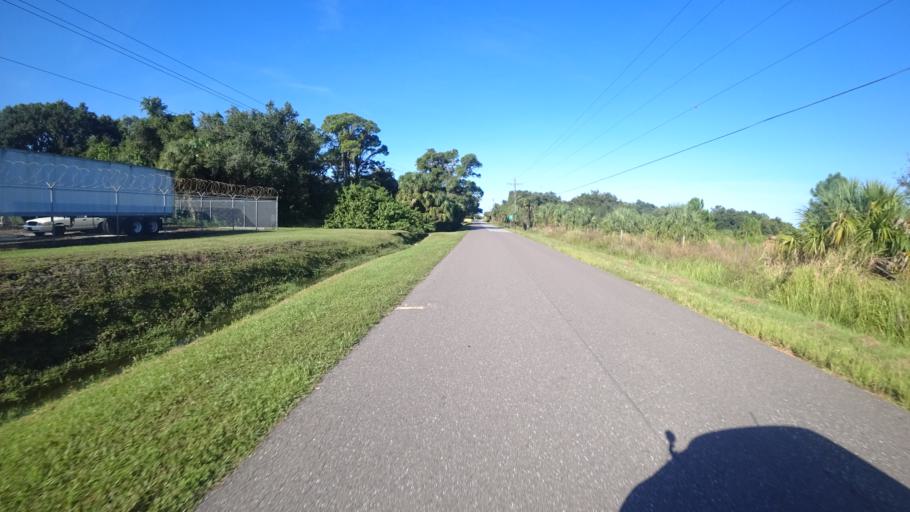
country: US
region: Florida
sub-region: Manatee County
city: Memphis
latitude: 27.6455
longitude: -82.5360
